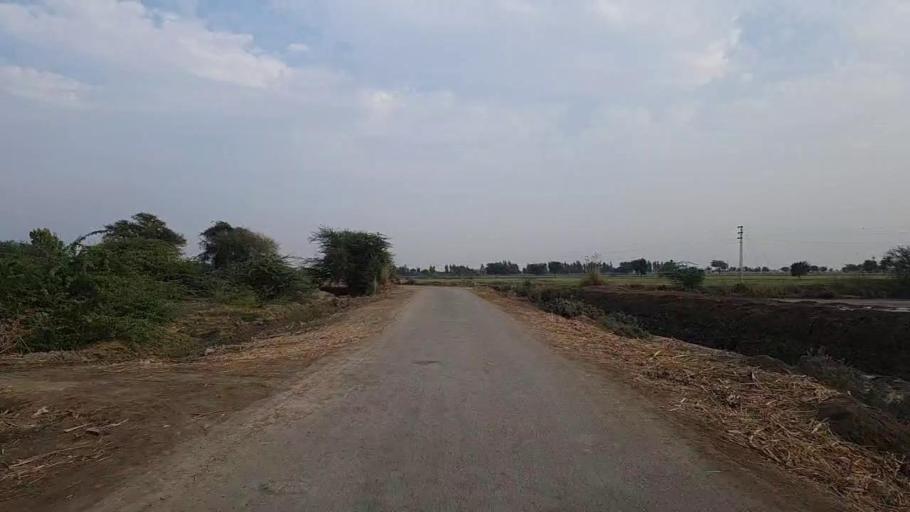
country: PK
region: Sindh
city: Pithoro
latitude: 25.4421
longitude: 69.2973
